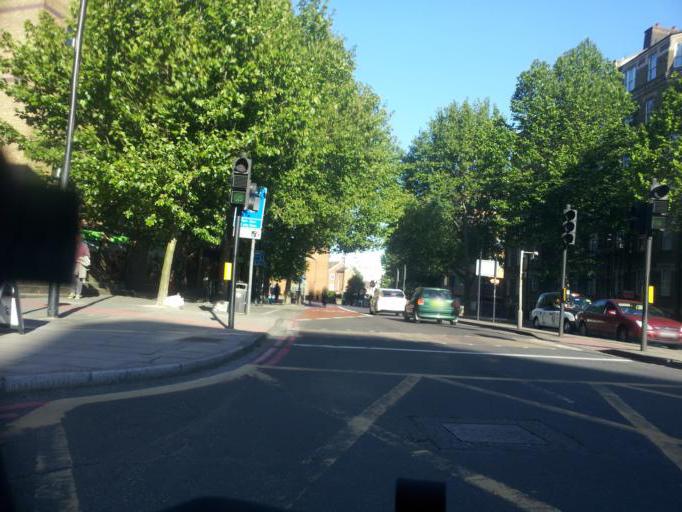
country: GB
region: England
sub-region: Greater London
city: City of London
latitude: 51.5004
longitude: -0.0741
